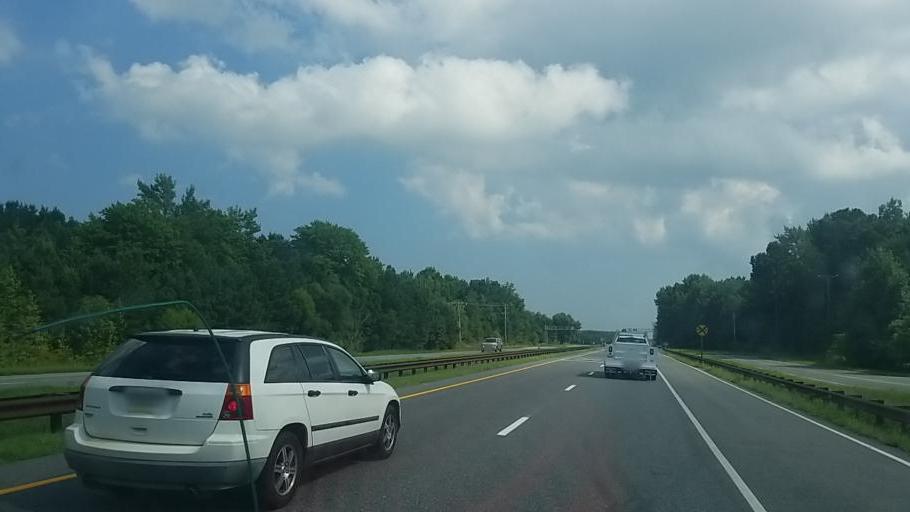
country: US
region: Delaware
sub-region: Sussex County
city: Selbyville
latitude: 38.4373
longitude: -75.2246
